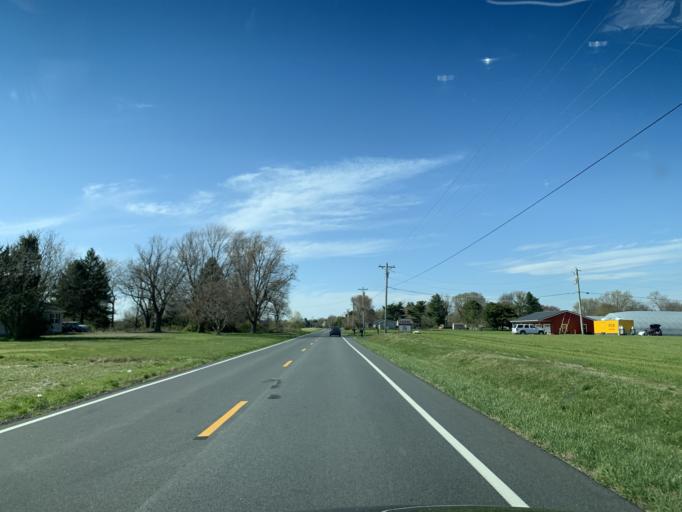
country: US
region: Delaware
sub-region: Kent County
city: Riverview
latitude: 39.0279
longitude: -75.5435
